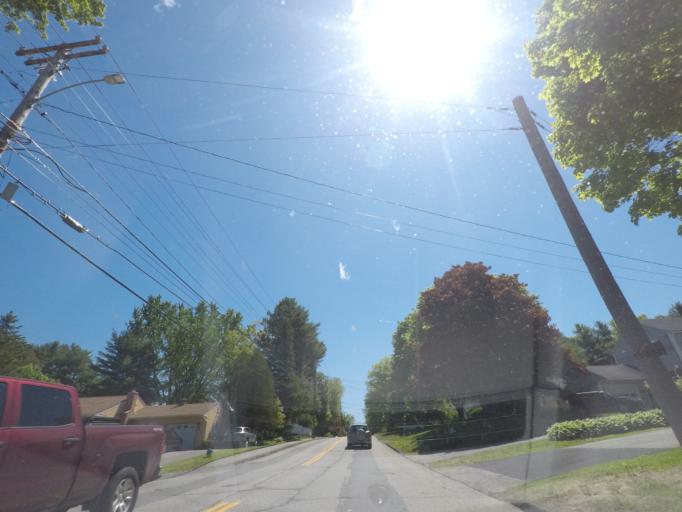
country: US
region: Maine
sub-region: Kennebec County
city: Augusta
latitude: 44.3197
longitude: -69.8107
